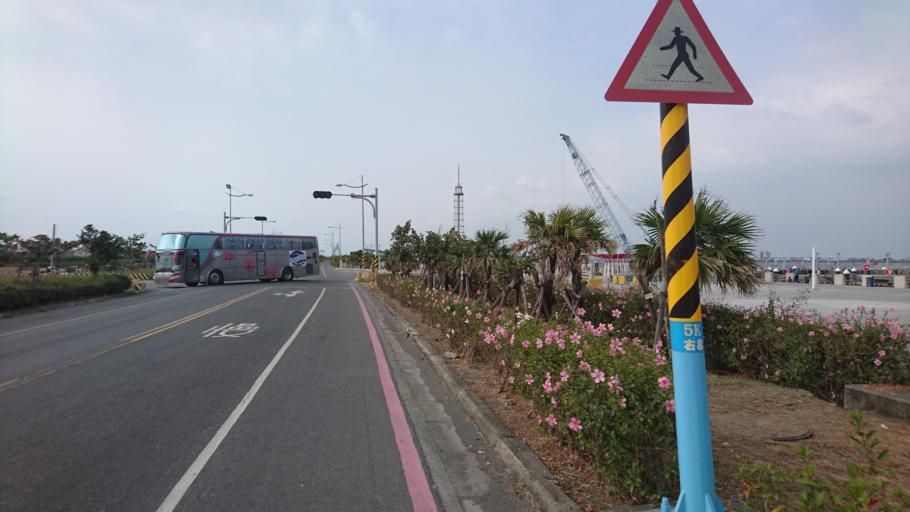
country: TW
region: Taiwan
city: Fengshan
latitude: 22.4374
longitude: 120.4751
